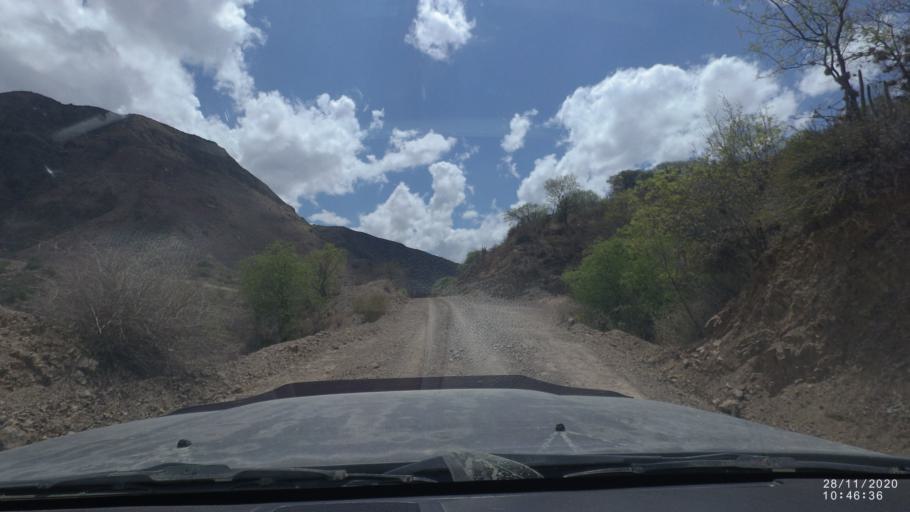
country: BO
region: Cochabamba
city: Capinota
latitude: -17.7878
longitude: -66.1281
